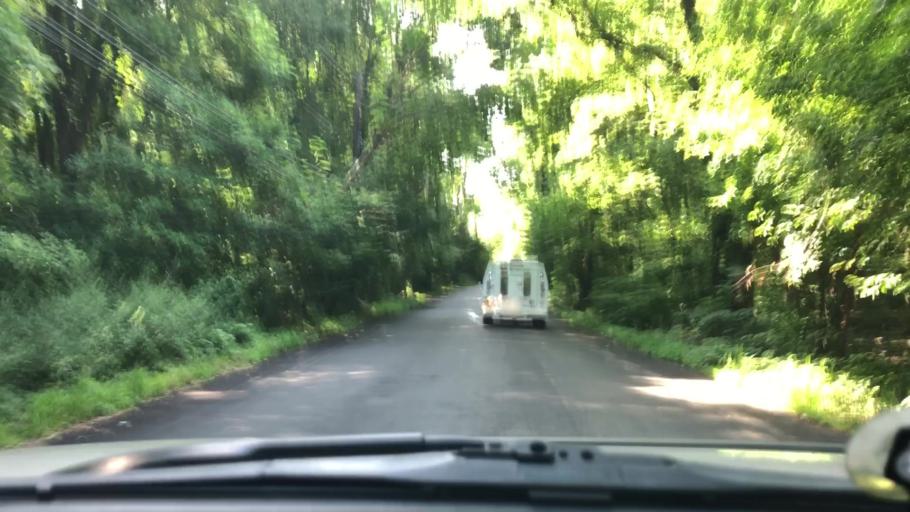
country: US
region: New York
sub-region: Richmond County
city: Staten Island
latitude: 40.5305
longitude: -74.1766
